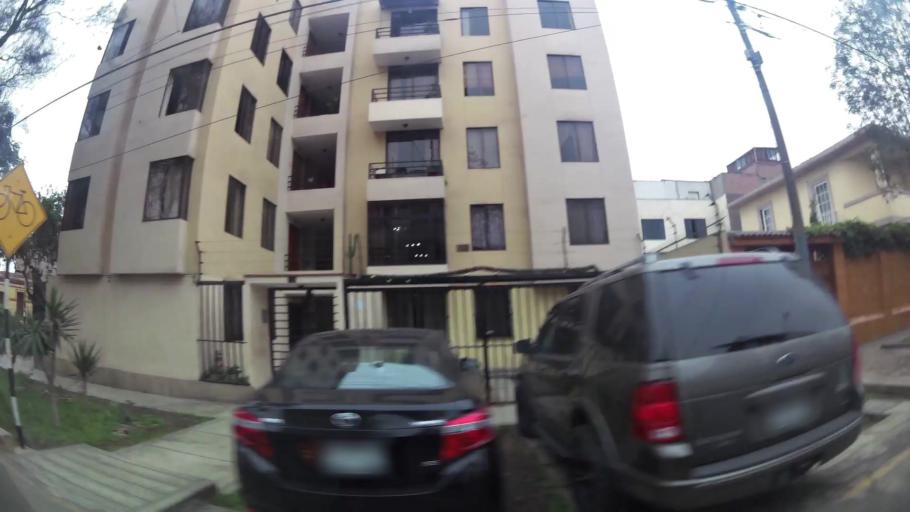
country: PE
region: Lima
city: Lima
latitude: -12.0705
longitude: -77.0469
